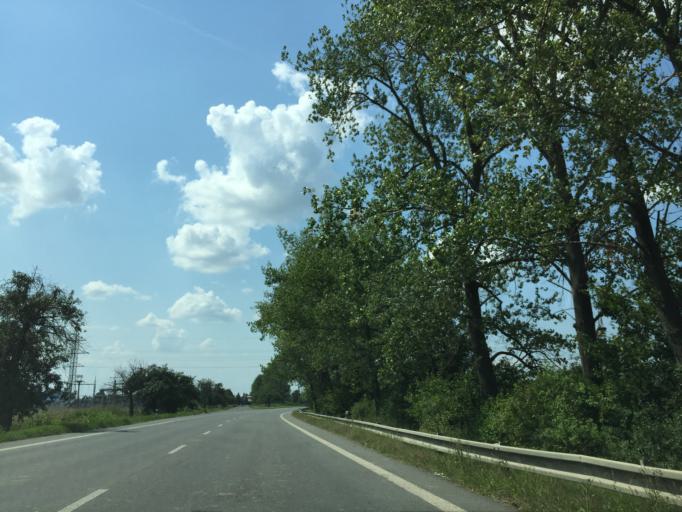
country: SK
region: Kosicky
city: Sobrance
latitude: 48.7411
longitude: 22.1936
